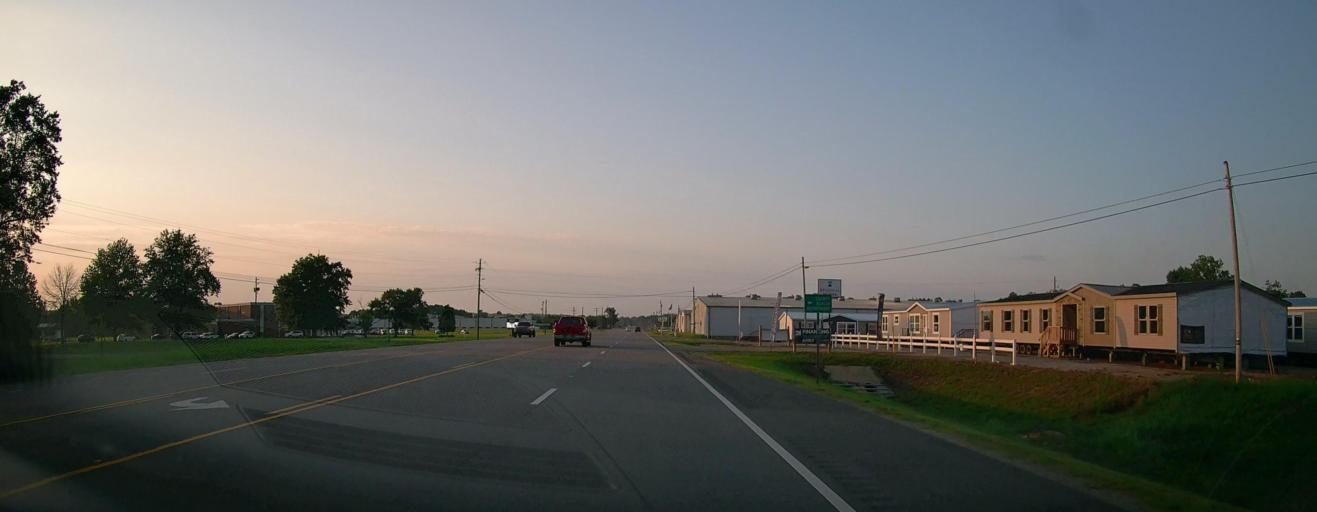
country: US
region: Alabama
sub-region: Marion County
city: Hamilton
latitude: 34.1080
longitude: -87.9891
